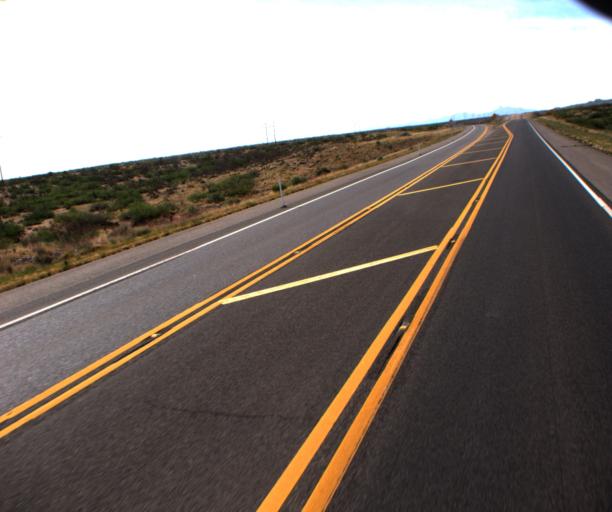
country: US
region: Arizona
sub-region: Graham County
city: Swift Trail Junction
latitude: 32.5955
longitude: -109.6850
